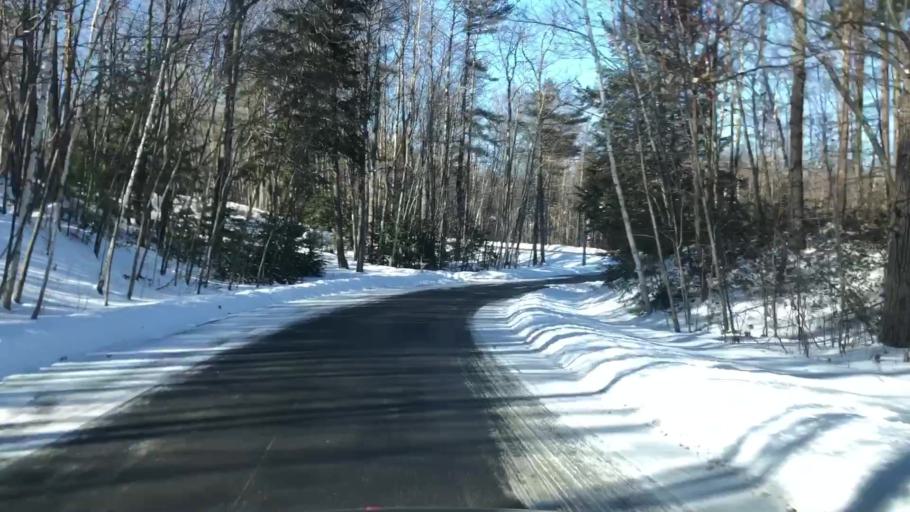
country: US
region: New Hampshire
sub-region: Hillsborough County
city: Bedford
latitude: 42.9442
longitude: -71.5480
